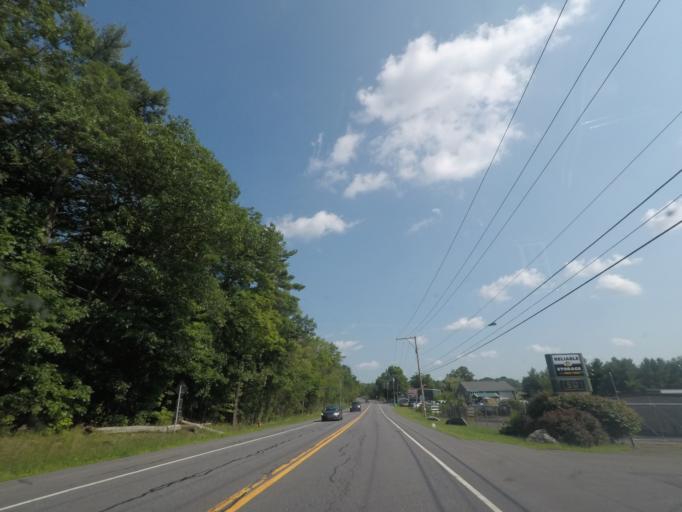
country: US
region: New York
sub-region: Rensselaer County
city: Nassau
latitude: 42.5319
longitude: -73.6576
